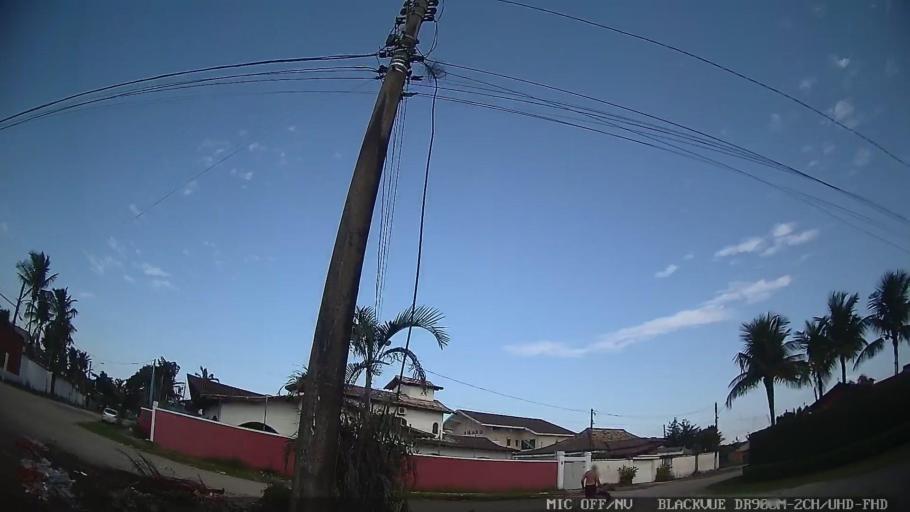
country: BR
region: Sao Paulo
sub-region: Guaruja
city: Guaruja
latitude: -23.9753
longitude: -46.2110
